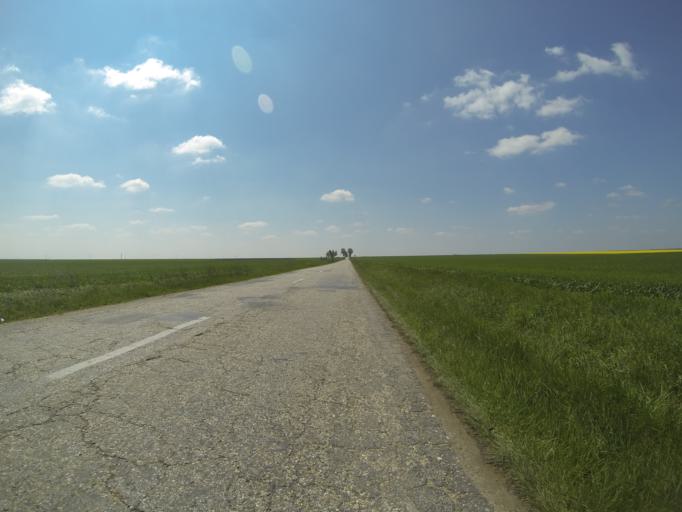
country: RO
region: Dolj
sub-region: Comuna Terpezita
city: Terpezita
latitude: 44.2685
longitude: 23.4759
